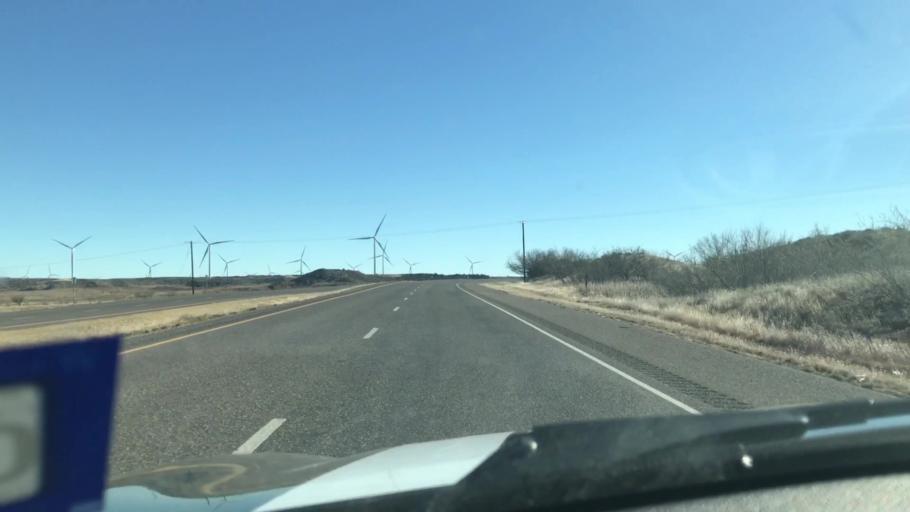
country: US
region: Texas
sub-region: Scurry County
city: Snyder
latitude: 32.9184
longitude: -101.0603
